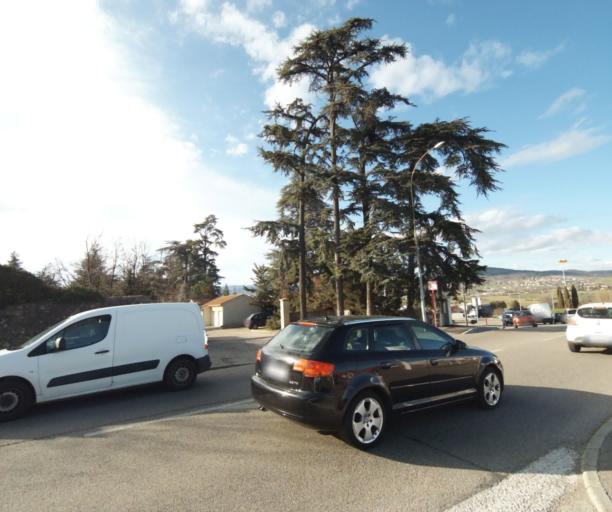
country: FR
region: Rhone-Alpes
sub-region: Departement de l'Ardeche
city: Davezieux
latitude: 45.2535
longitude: 4.6878
